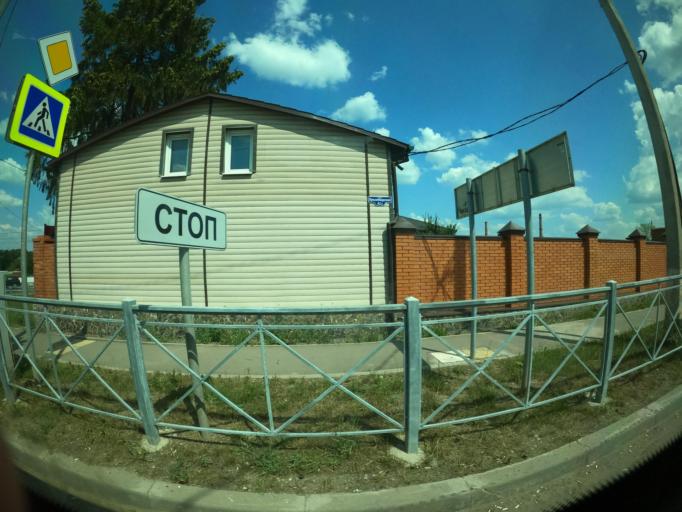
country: RU
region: Moskovskaya
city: Serpukhov
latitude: 54.9188
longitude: 37.3876
